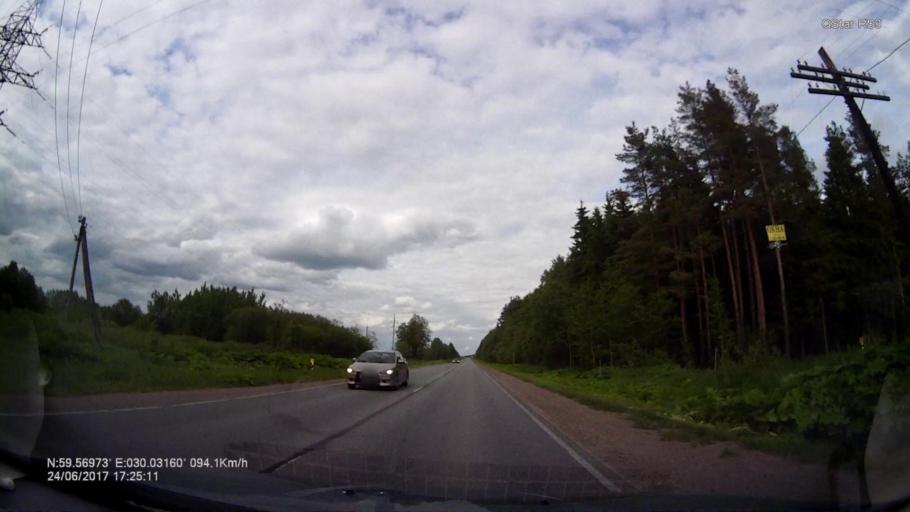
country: RU
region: Leningrad
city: Mariyenburg
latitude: 59.5700
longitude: 30.0322
